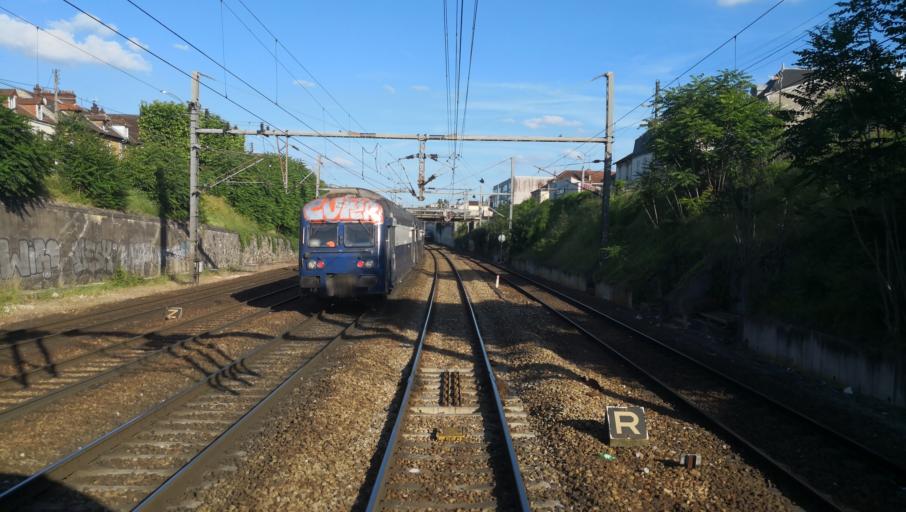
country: FR
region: Ile-de-France
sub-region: Departement des Yvelines
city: Mantes-la-Jolie
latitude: 48.9855
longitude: 1.7111
